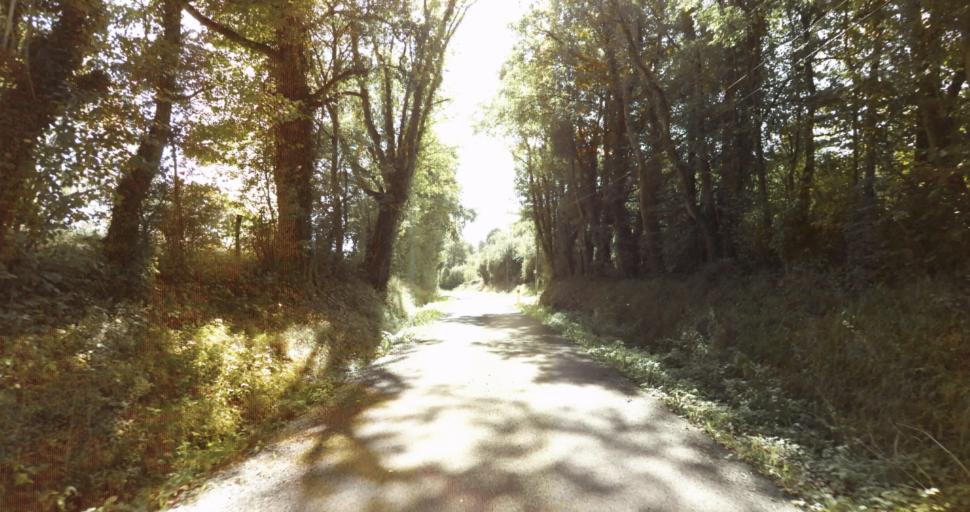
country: FR
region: Lower Normandy
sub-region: Departement de l'Orne
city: Gace
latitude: 48.7333
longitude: 0.2371
